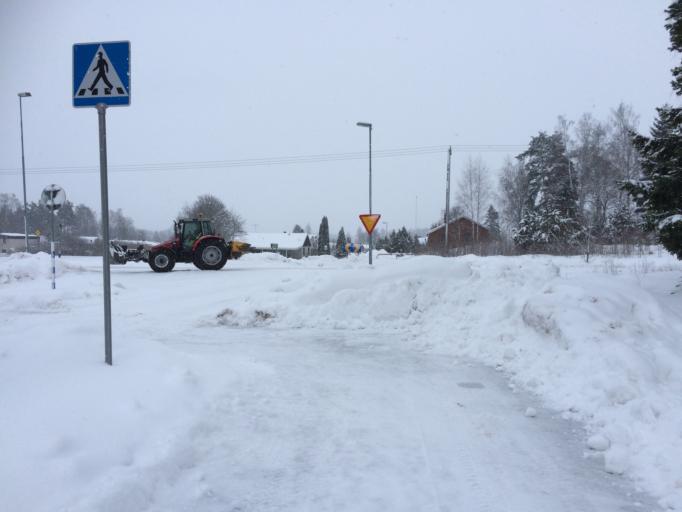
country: SE
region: Vaestmanland
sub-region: Hallstahammars Kommun
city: Hallstahammar
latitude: 59.6257
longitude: 16.2451
